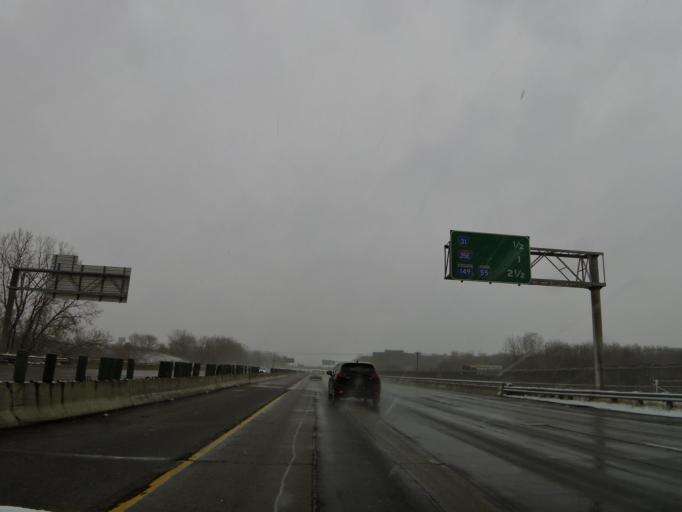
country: US
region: Minnesota
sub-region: Dakota County
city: Mendota Heights
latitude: 44.8612
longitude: -93.1779
